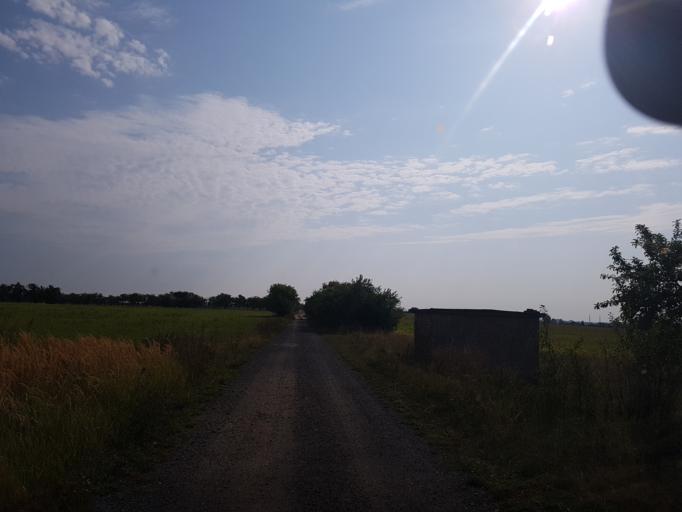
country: DE
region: Brandenburg
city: Hohenleipisch
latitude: 51.4972
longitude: 13.5362
